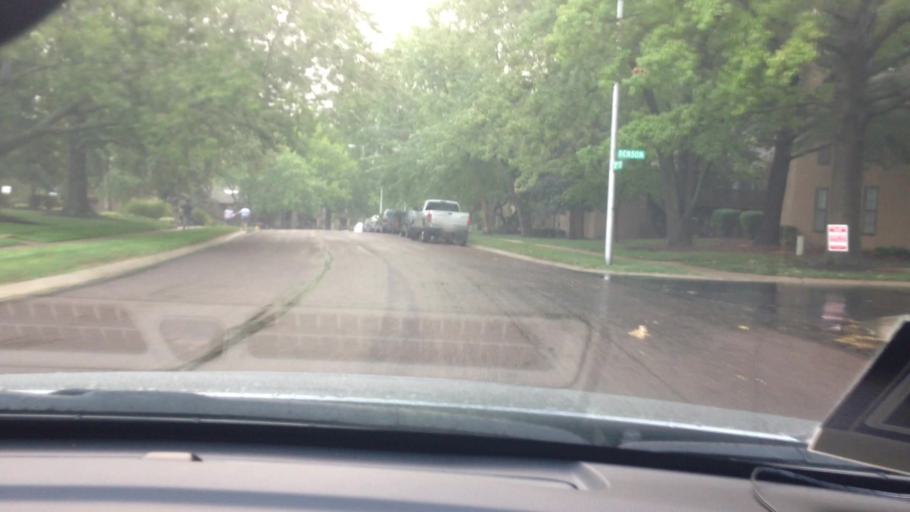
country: US
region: Kansas
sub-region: Johnson County
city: Overland Park
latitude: 38.9437
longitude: -94.6887
